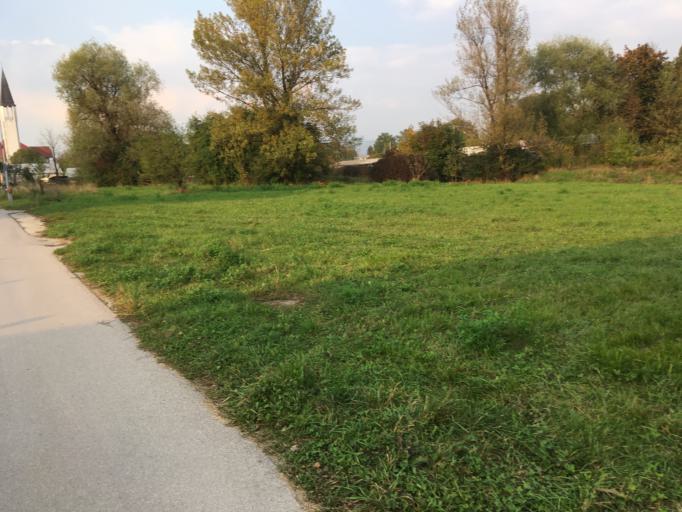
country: SI
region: Domzale
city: Vir
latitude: 46.1536
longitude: 14.6062
